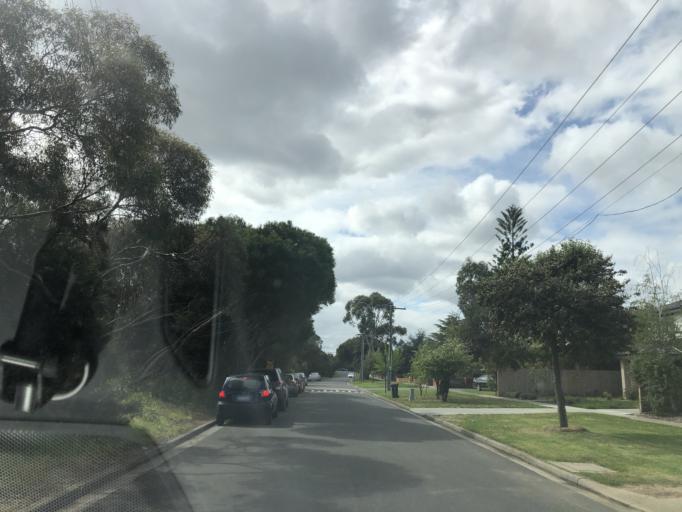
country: AU
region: Victoria
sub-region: Monash
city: Chadstone
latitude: -37.8849
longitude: 145.0932
